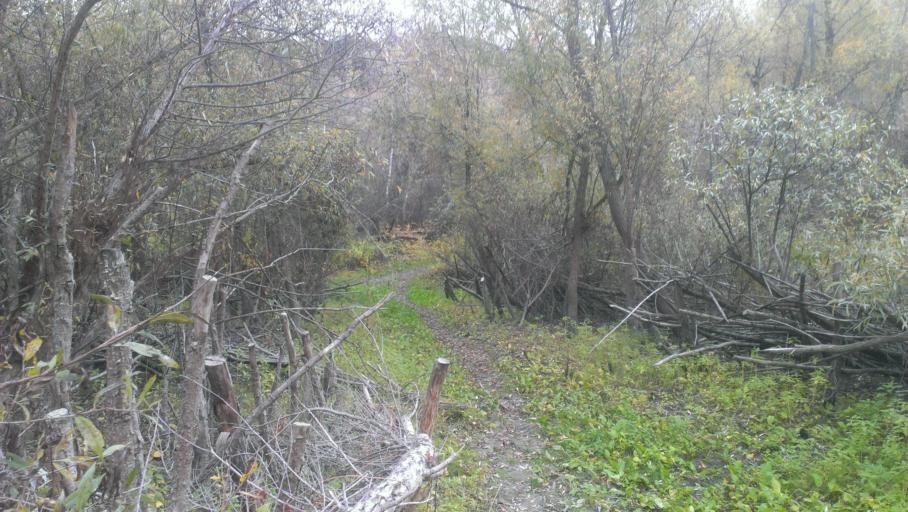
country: RU
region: Altai Krai
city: Nauchnyy Gorodok
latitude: 53.4265
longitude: 83.5037
